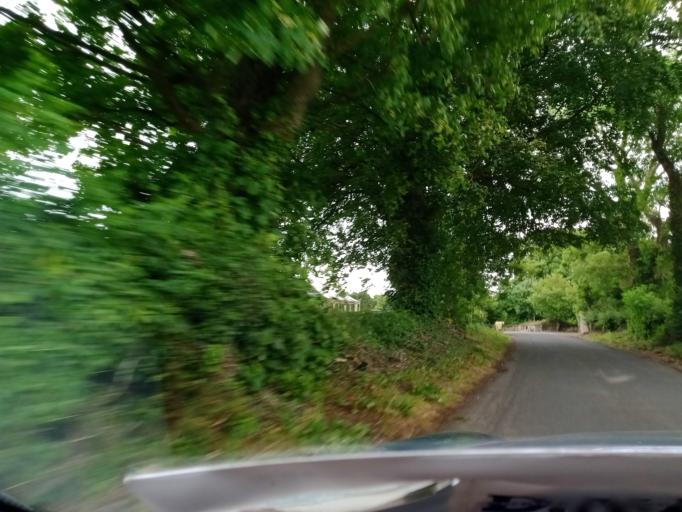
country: IE
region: Leinster
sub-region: Kilkenny
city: Thomastown
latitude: 52.5575
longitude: -7.2048
